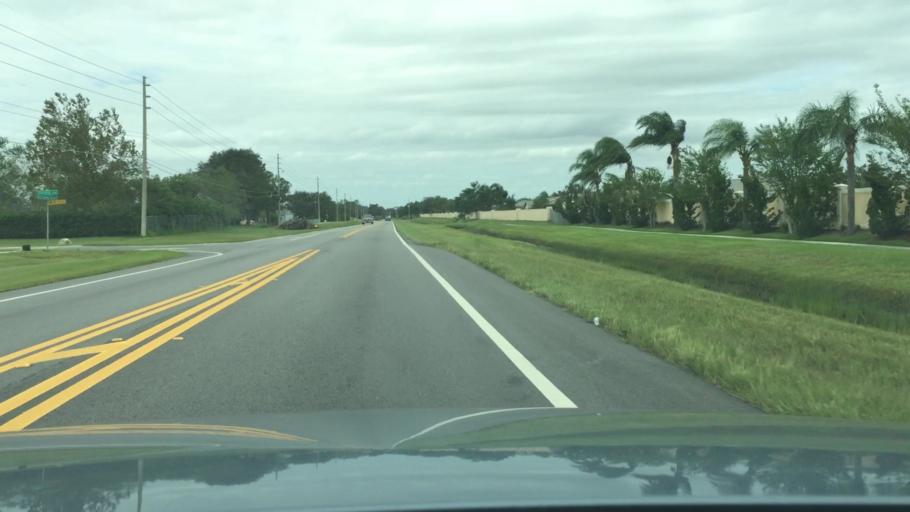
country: US
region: Florida
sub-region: Osceola County
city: Saint Cloud
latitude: 28.2028
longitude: -81.2984
